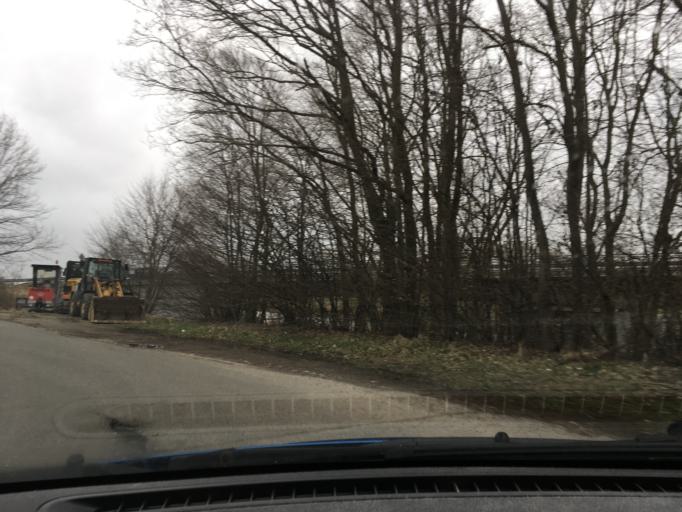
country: DE
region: Lower Saxony
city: Winsen
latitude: 53.3754
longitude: 10.2430
